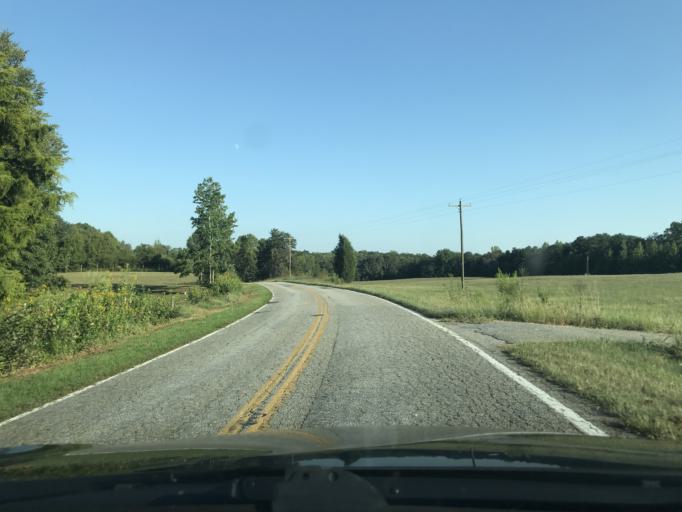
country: US
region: South Carolina
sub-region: Spartanburg County
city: Mayo
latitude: 35.1094
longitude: -81.7843
